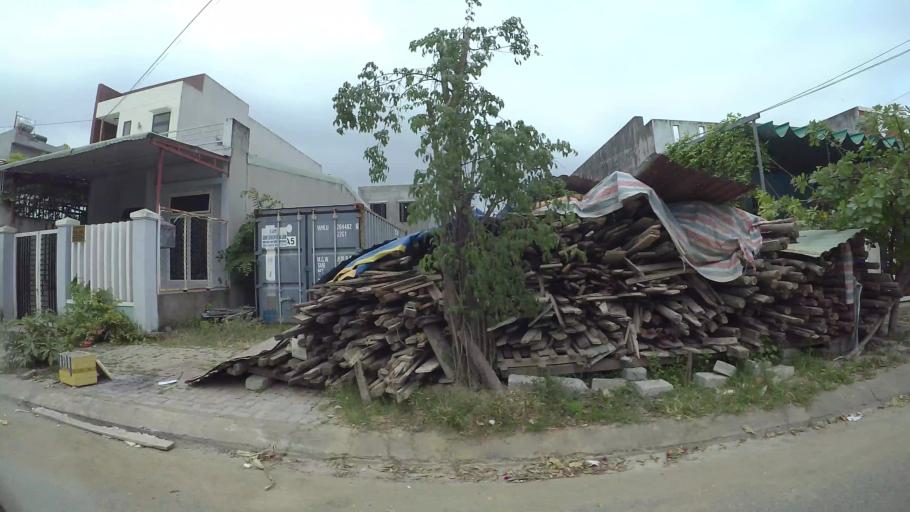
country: VN
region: Da Nang
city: Lien Chieu
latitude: 16.0451
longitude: 108.1698
